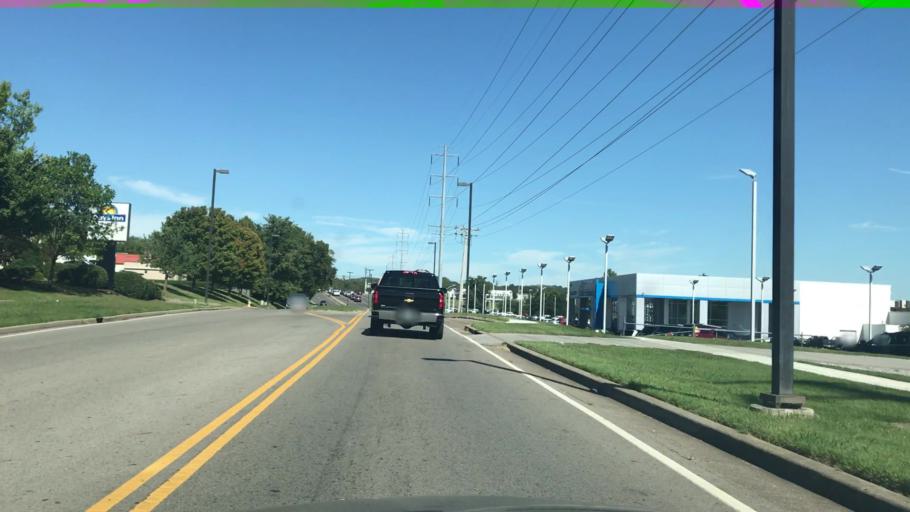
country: US
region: Tennessee
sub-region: Williamson County
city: Franklin
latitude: 35.9103
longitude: -86.8220
